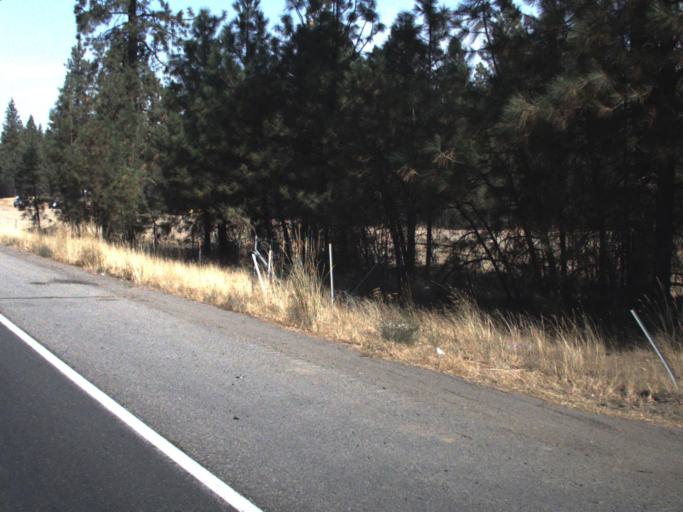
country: US
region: Washington
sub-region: Spokane County
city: Country Homes
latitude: 47.7633
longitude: -117.3887
